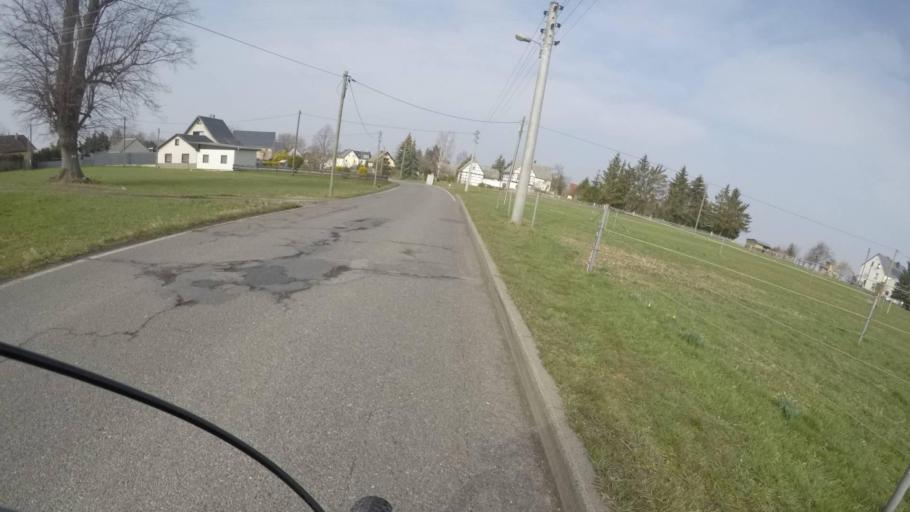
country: DE
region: Saxony
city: Niederfrohna
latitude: 50.8867
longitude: 12.6982
